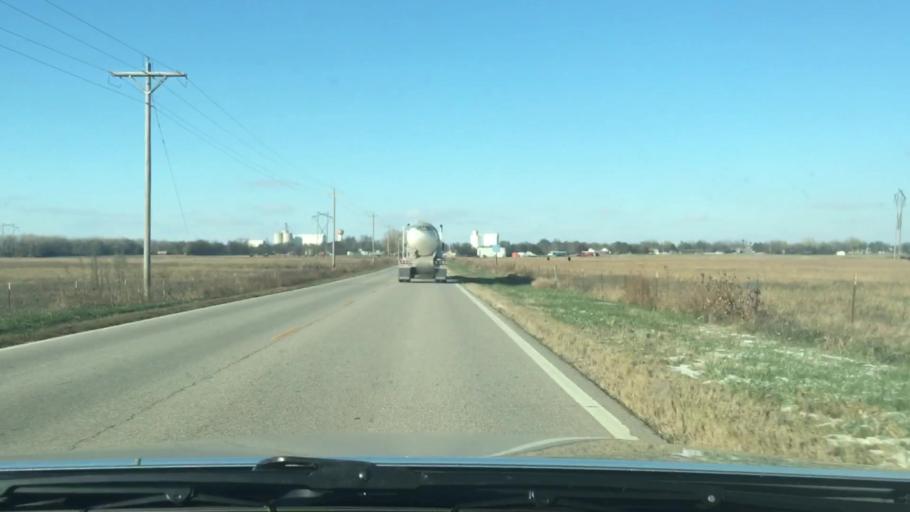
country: US
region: Kansas
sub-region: Rice County
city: Sterling
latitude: 38.1934
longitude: -98.2066
